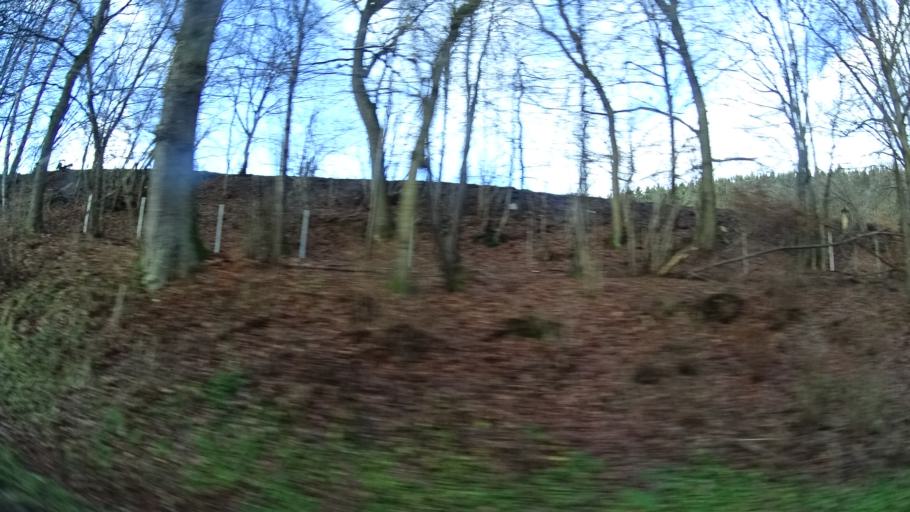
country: DE
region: Thuringia
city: Wernshausen
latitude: 50.7247
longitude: 10.3304
